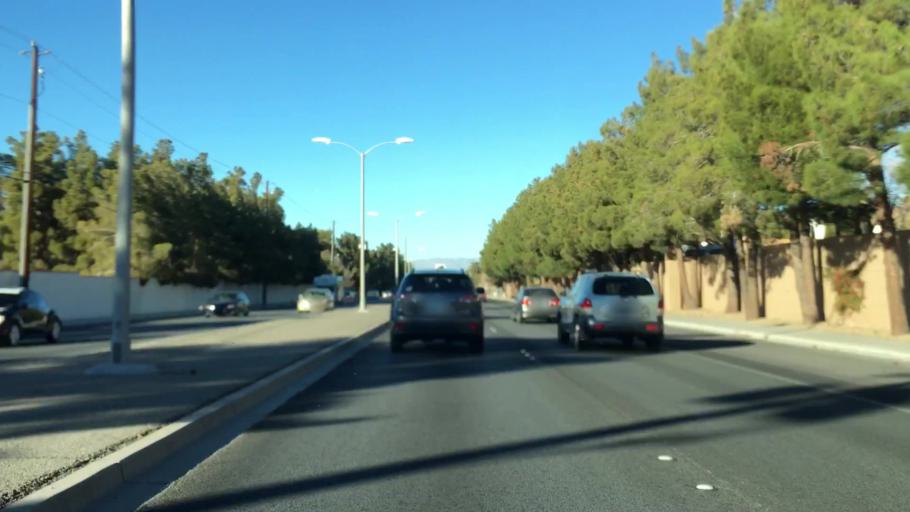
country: US
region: Nevada
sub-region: Clark County
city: Whitney
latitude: 36.0592
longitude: -115.1004
